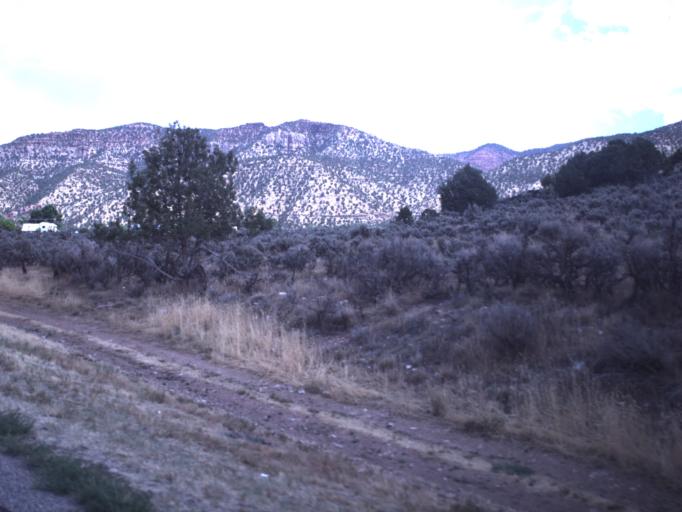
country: US
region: Utah
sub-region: Iron County
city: Parowan
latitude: 37.8810
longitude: -112.7769
